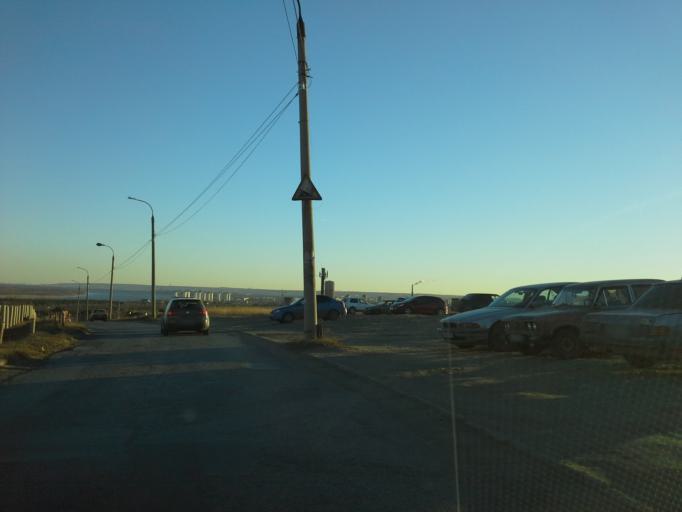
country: RU
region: Volgograd
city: Volgograd
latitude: 48.6408
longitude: 44.4211
